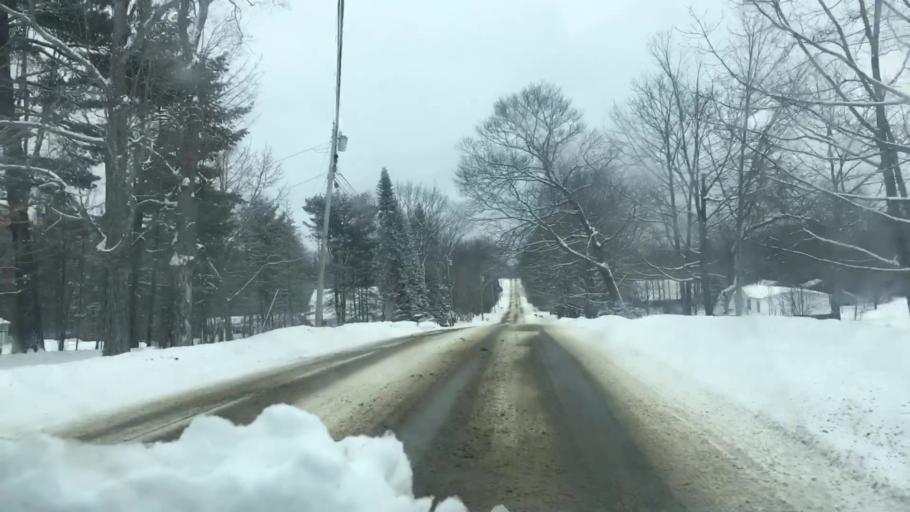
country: US
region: Maine
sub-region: Penobscot County
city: Bradford
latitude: 45.0112
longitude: -68.9968
